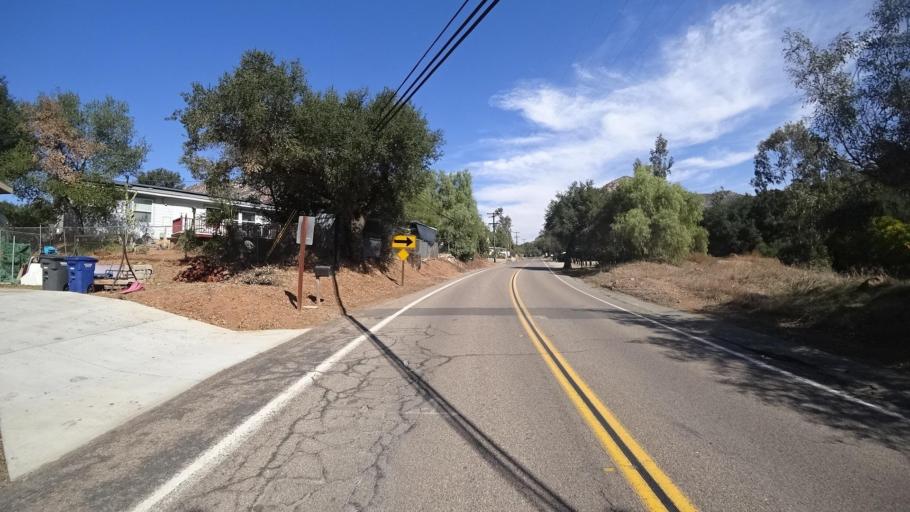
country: US
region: California
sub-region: San Diego County
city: Harbison Canyon
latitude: 32.8199
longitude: -116.8302
